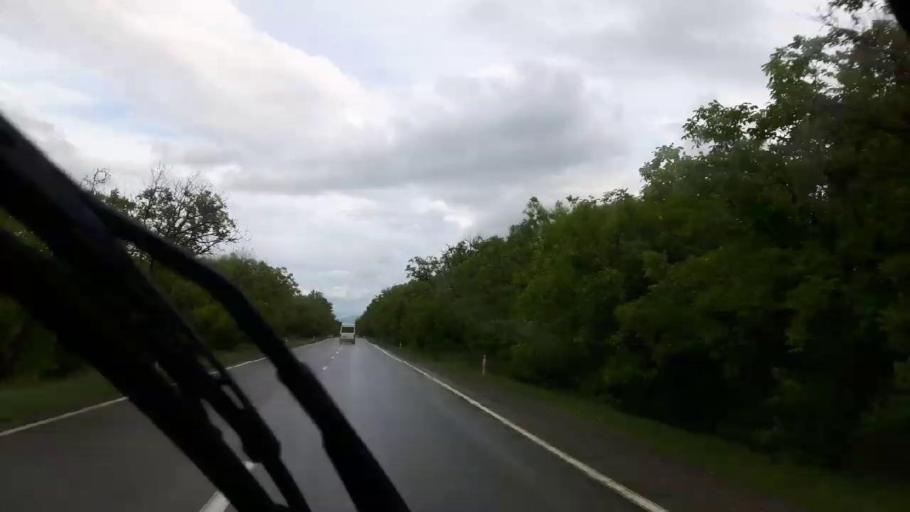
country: GE
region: Shida Kartli
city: Kaspi
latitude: 41.9566
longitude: 44.4881
